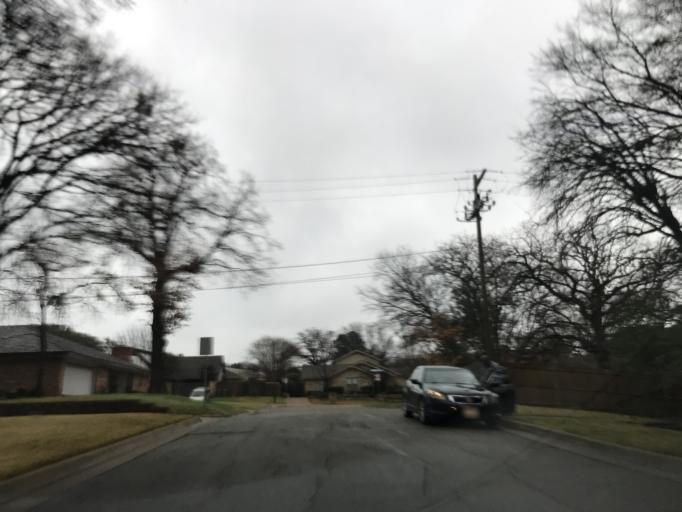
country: US
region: Texas
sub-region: Tarrant County
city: Arlington
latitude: 32.7735
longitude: -97.1088
